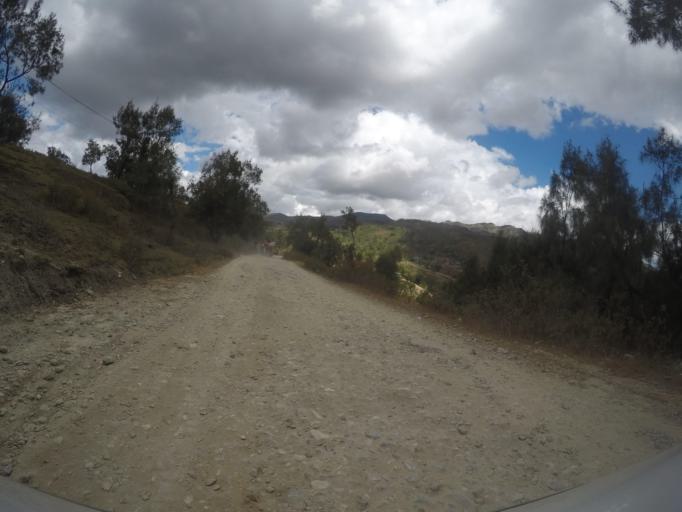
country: TL
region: Baucau
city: Baucau
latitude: -8.5011
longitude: 126.6789
